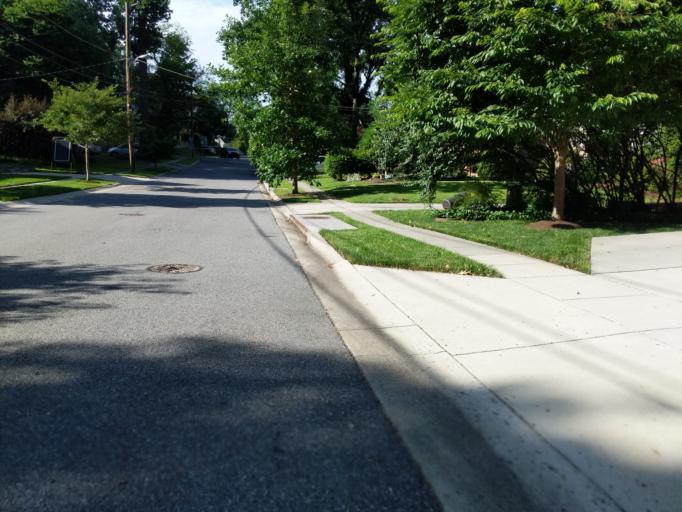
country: US
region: Maryland
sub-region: Montgomery County
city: Bethesda
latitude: 39.0011
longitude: -77.1123
